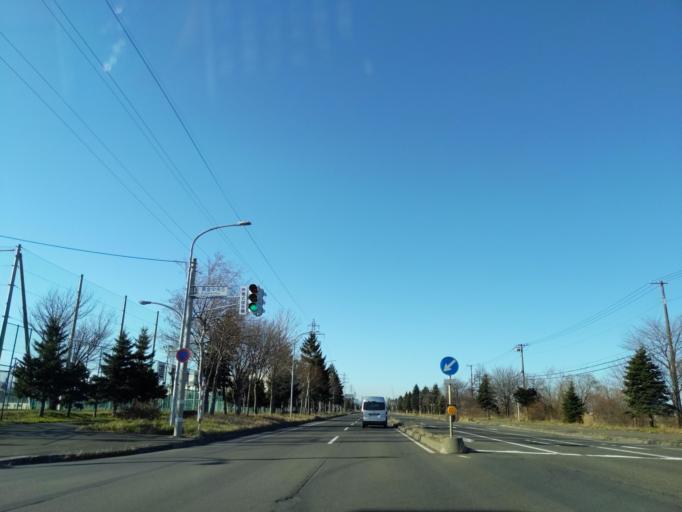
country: JP
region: Hokkaido
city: Kitahiroshima
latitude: 42.8924
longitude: 141.5966
